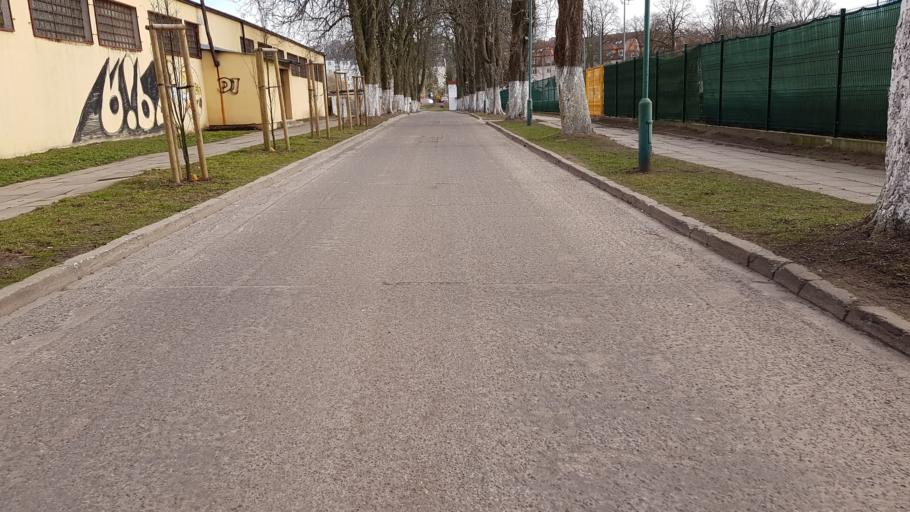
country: PL
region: West Pomeranian Voivodeship
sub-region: Powiat gryfinski
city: Gryfino
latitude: 53.2493
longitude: 14.4844
